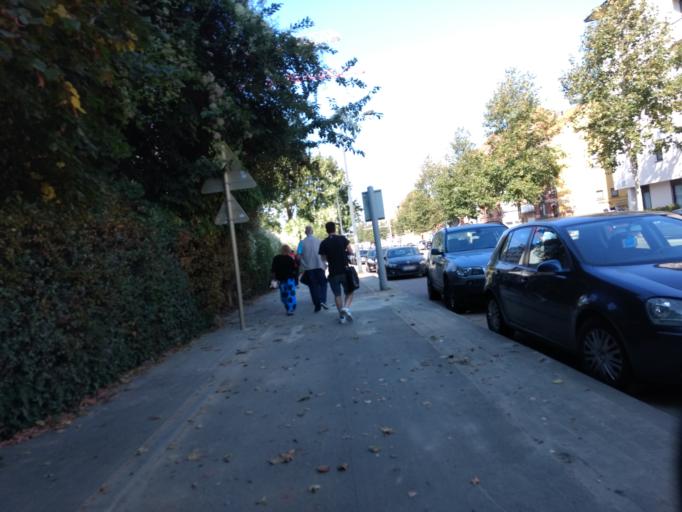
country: BE
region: Brussels Capital
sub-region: Bruxelles-Capitale
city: Brussels
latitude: 50.8223
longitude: 4.4009
